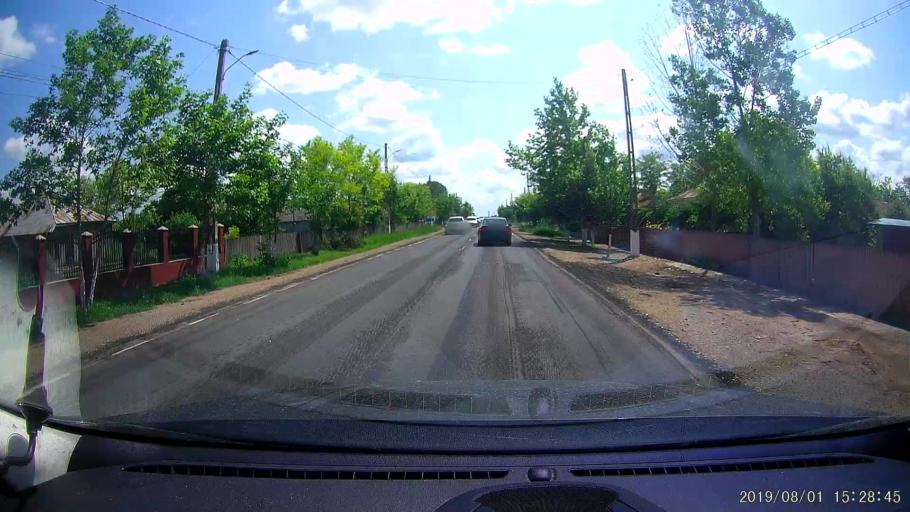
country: RO
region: Braila
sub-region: Comuna Viziru
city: Viziru
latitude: 44.9907
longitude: 27.7062
